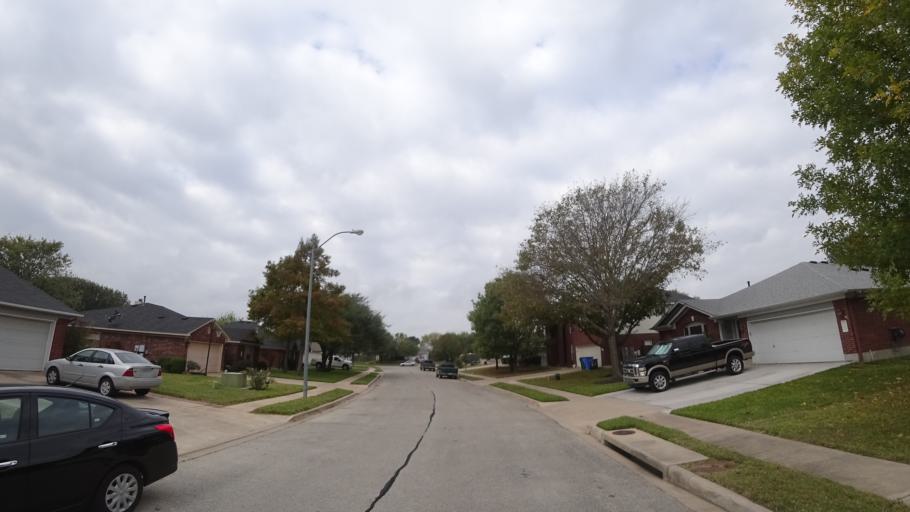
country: US
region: Texas
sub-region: Travis County
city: Pflugerville
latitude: 30.4389
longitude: -97.6072
